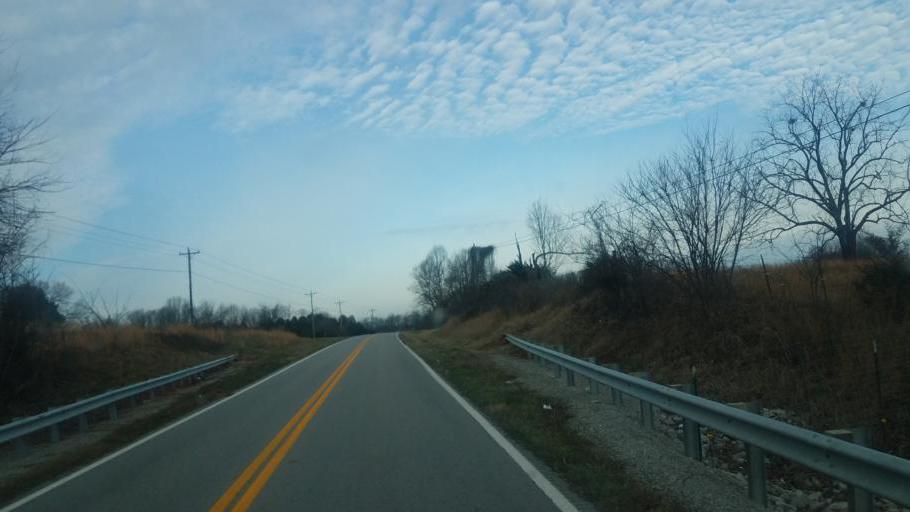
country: US
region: Kentucky
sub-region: Clinton County
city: Albany
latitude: 36.7584
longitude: -85.1551
